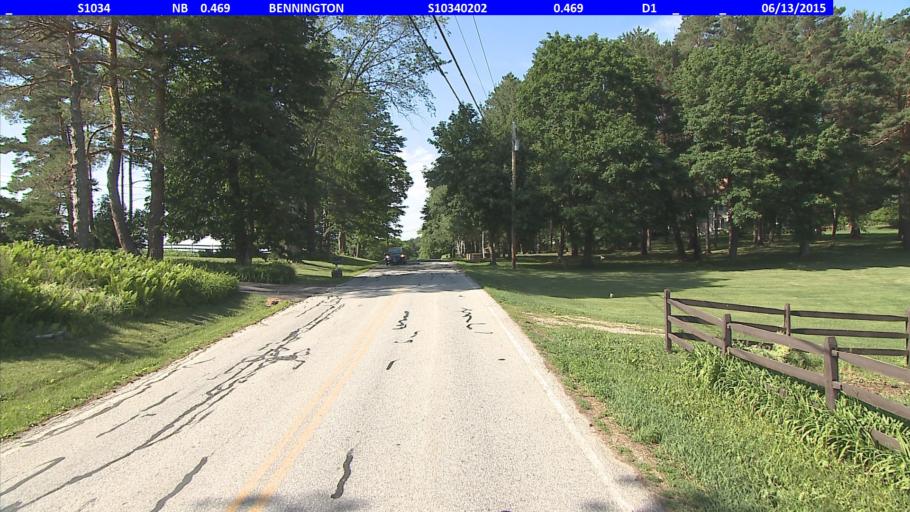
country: US
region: Vermont
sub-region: Bennington County
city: Bennington
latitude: 42.8588
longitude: -73.2061
